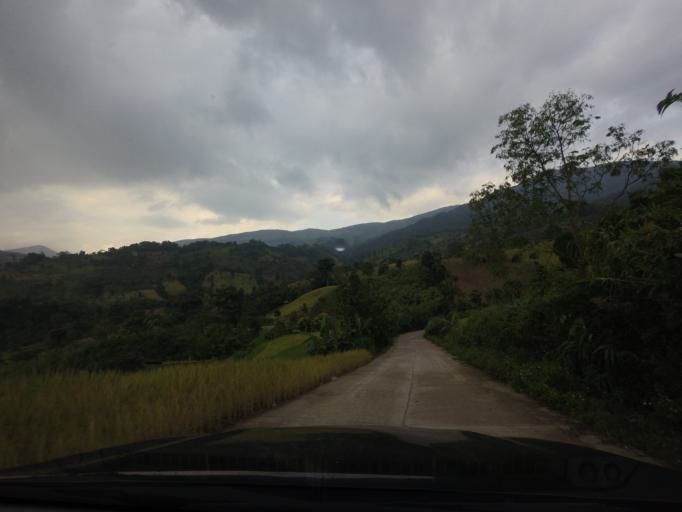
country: TH
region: Nan
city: Bo Kluea
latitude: 19.3512
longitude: 101.1701
